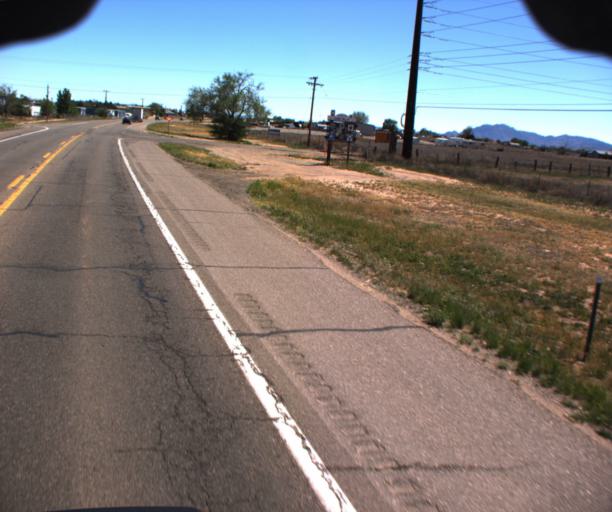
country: US
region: Arizona
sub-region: Yavapai County
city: Chino Valley
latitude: 34.8054
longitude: -112.4505
